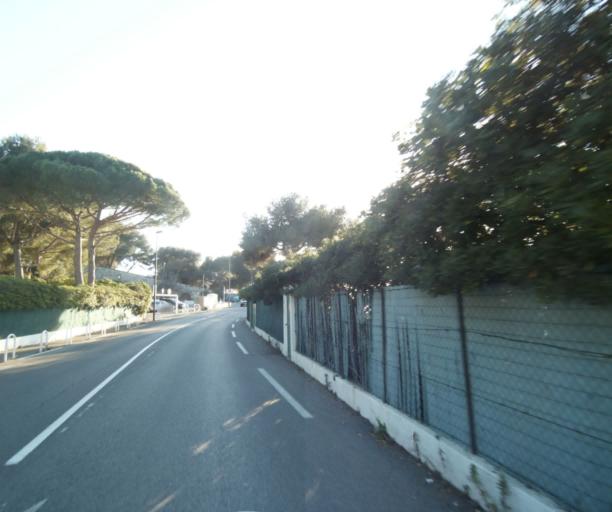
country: FR
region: Provence-Alpes-Cote d'Azur
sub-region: Departement des Alpes-Maritimes
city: Antibes
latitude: 43.5501
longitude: 7.1186
